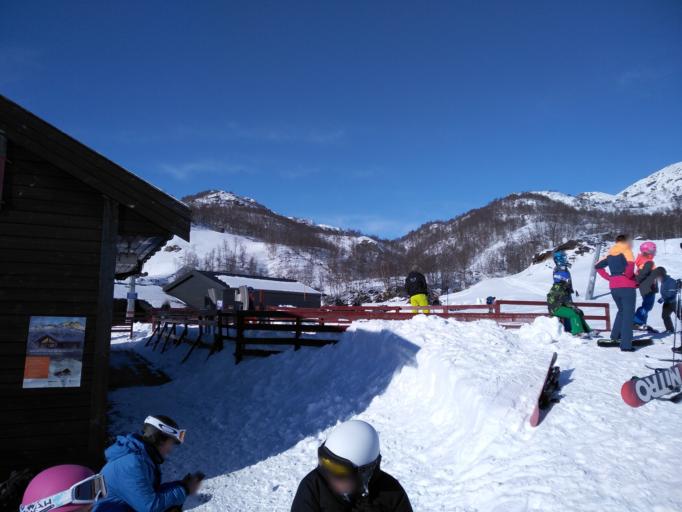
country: NO
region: Vest-Agder
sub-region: Sirdal
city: Tonstad
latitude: 58.9595
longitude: 6.9445
